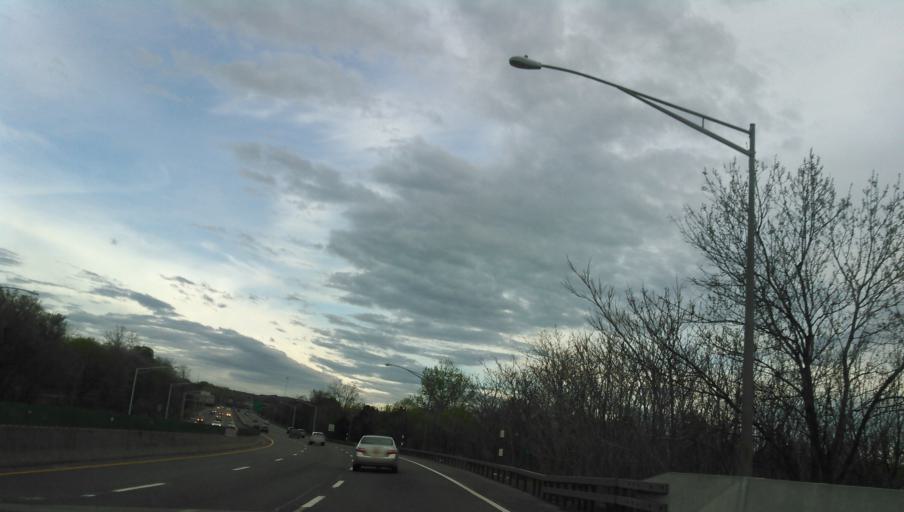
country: US
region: New York
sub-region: Onondaga County
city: Syracuse
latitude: 43.0344
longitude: -76.1431
